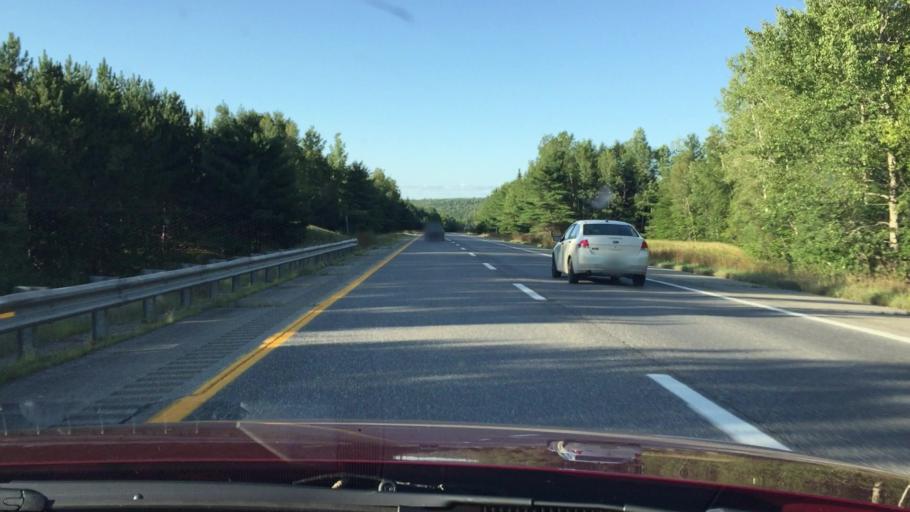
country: US
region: Maine
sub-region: Penobscot County
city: Medway
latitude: 45.6247
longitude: -68.5067
